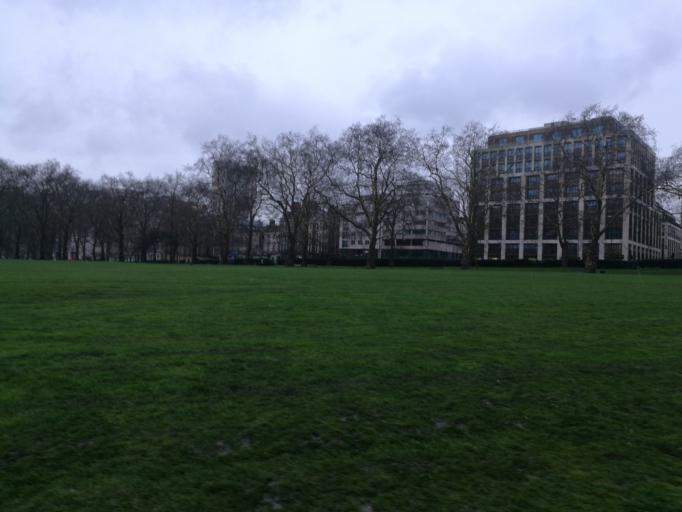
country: GB
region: England
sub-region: Greater London
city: London
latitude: 51.5058
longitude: -0.1422
